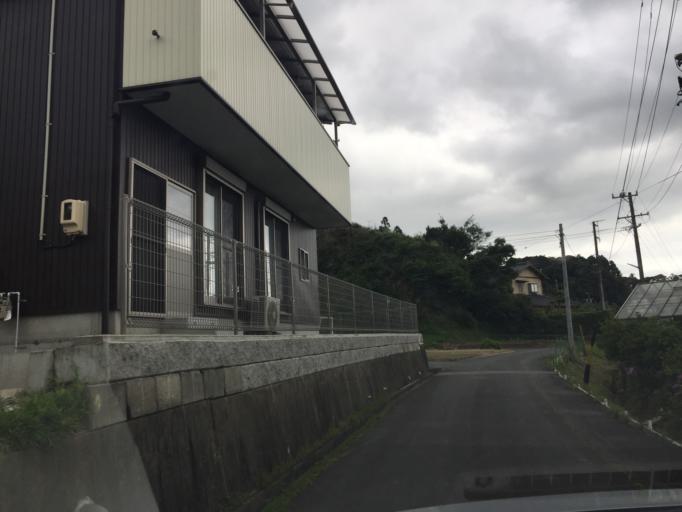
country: JP
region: Shizuoka
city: Fukuroi
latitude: 34.7800
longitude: 137.9389
